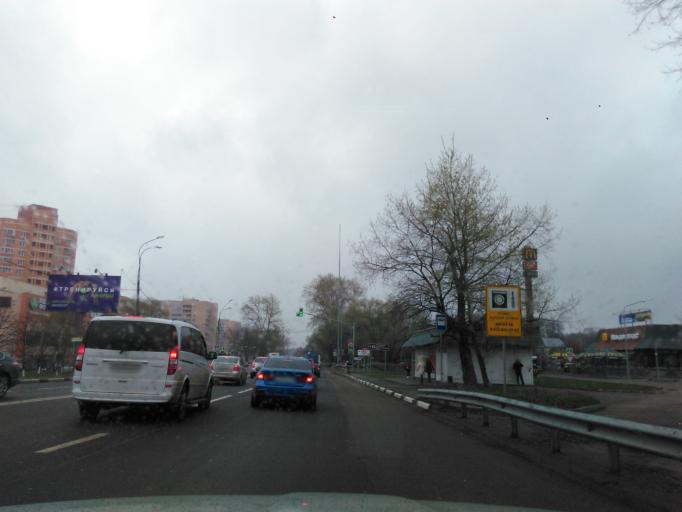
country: RU
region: Moskovskaya
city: Krasnogorsk
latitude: 55.8300
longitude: 37.3057
